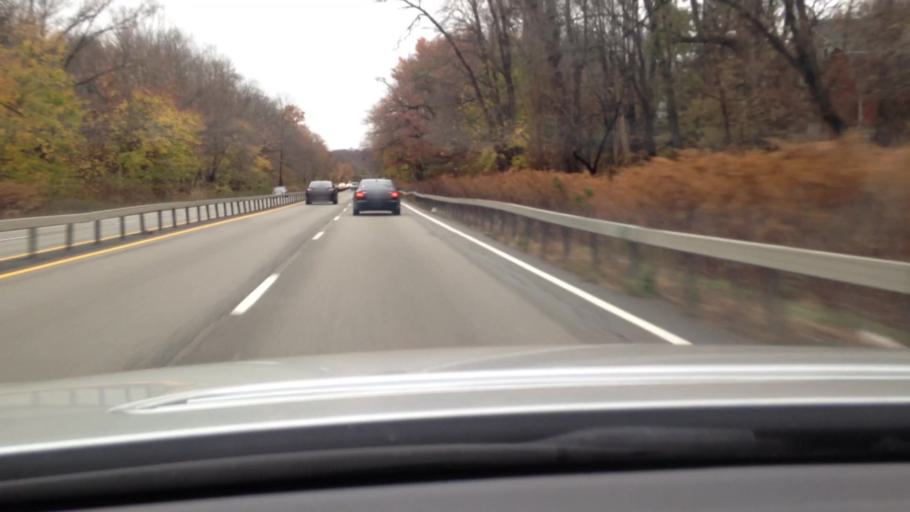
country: US
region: New York
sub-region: Westchester County
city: Briarcliff Manor
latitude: 41.1392
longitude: -73.8206
